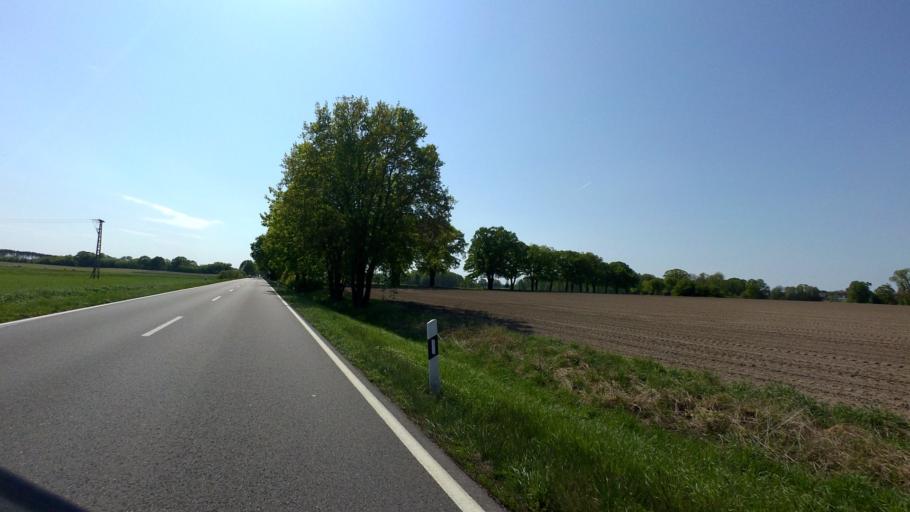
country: DE
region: Brandenburg
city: Neu Zauche
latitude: 52.0261
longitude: 14.0861
